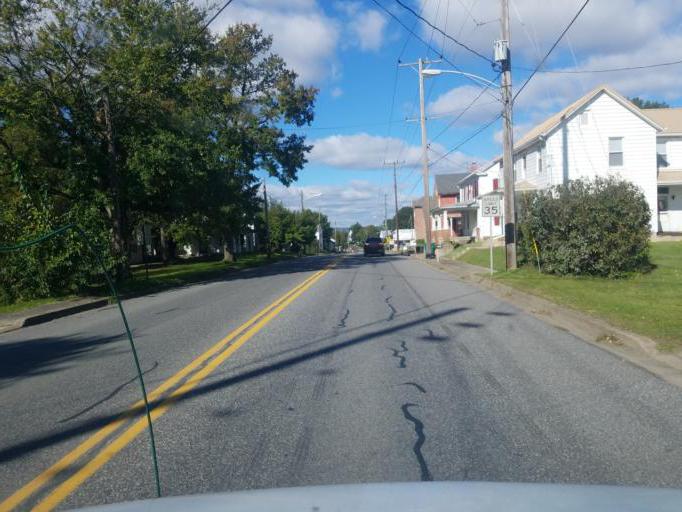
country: US
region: Pennsylvania
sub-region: Franklin County
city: Greencastle
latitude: 39.8045
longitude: -77.8041
